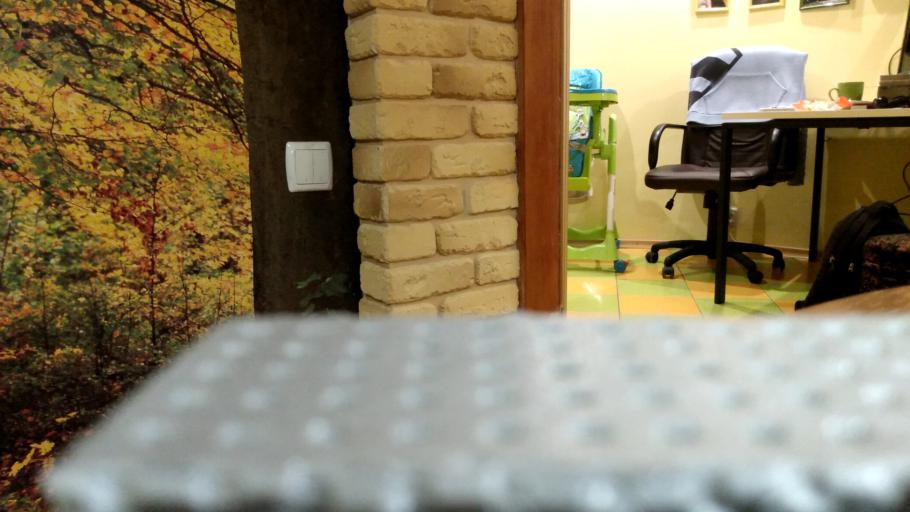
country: RU
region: Republic of Karelia
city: Pudozh
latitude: 61.8410
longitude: 37.6570
